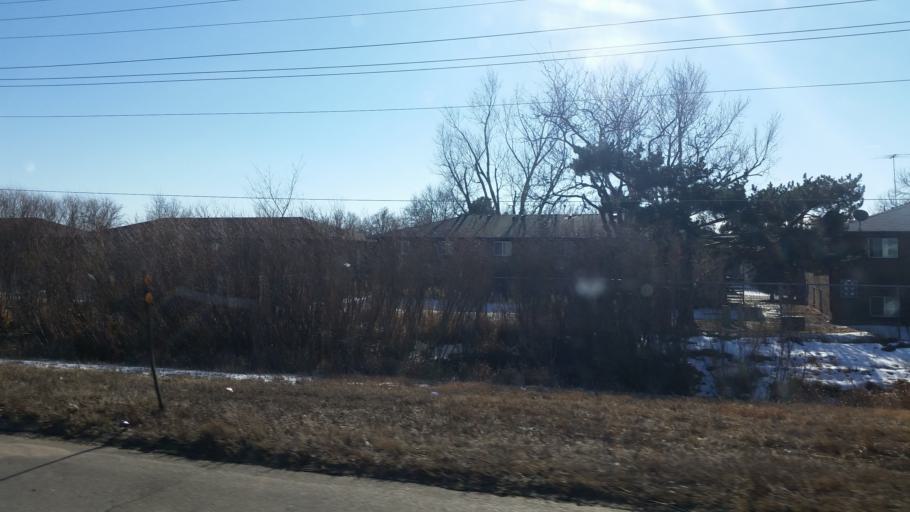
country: US
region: Colorado
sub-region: Weld County
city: Evans
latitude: 40.3915
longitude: -104.6943
